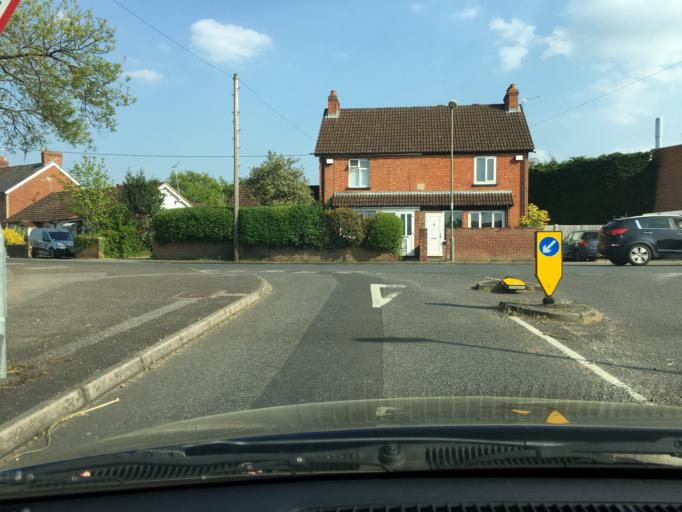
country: GB
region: England
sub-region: Bracknell Forest
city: Sandhurst
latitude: 51.3371
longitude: -0.7968
